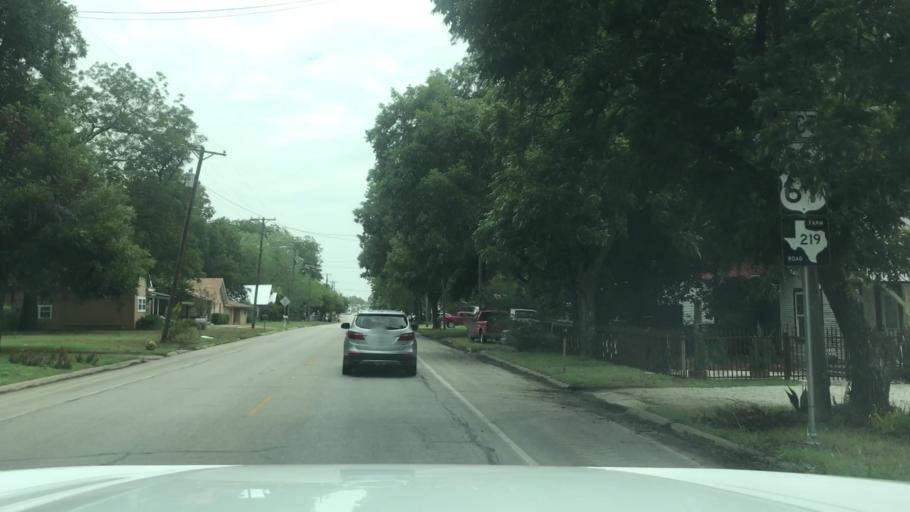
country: US
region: Texas
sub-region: Erath County
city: Dublin
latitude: 32.0863
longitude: -98.3473
